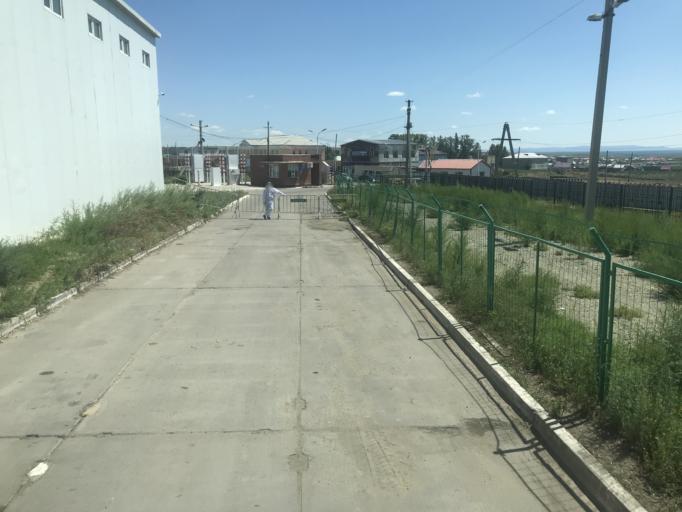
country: MN
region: Selenge
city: Altanbulag
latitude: 50.3208
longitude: 106.4894
